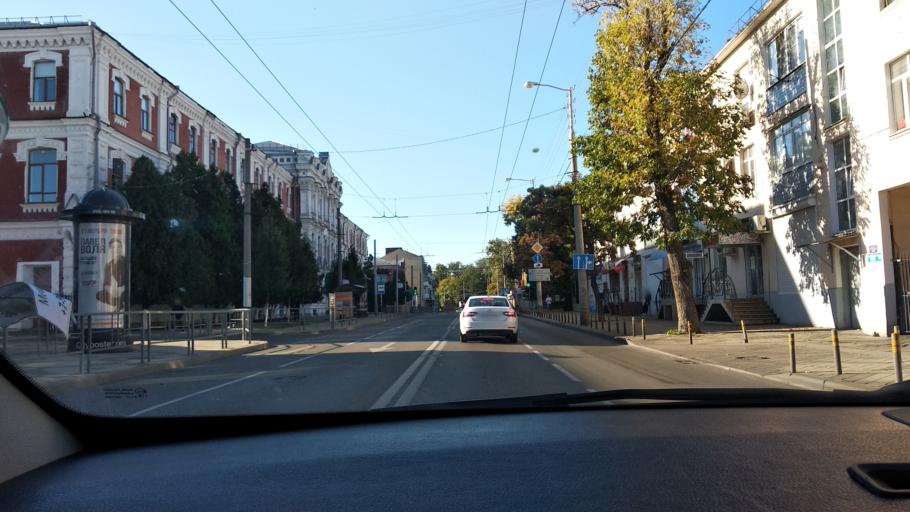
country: RU
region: Krasnodarskiy
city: Krasnodar
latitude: 45.0160
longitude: 38.9744
